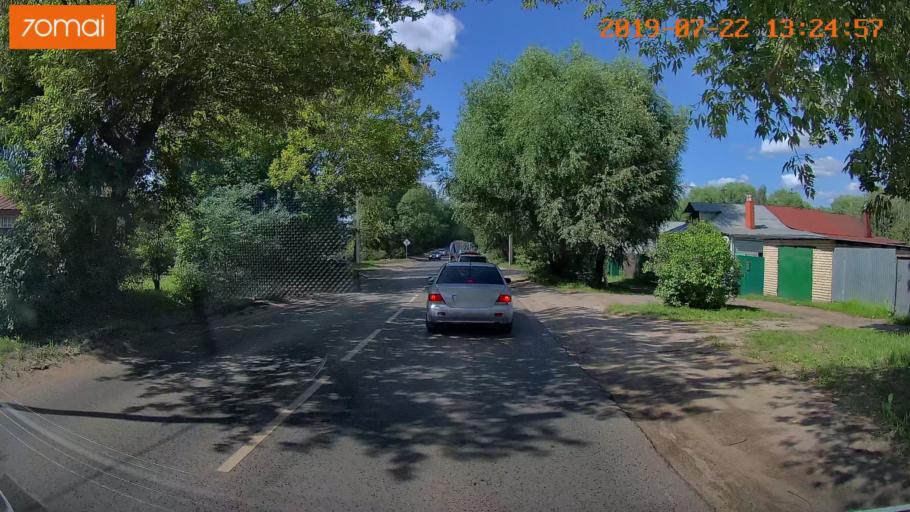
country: RU
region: Ivanovo
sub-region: Gorod Ivanovo
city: Ivanovo
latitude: 57.0269
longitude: 40.9509
